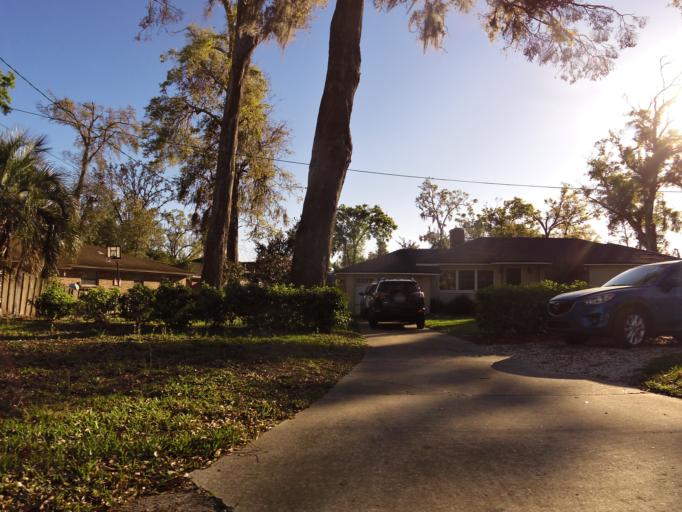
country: US
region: Florida
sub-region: Duval County
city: Jacksonville
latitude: 30.2747
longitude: -81.6516
